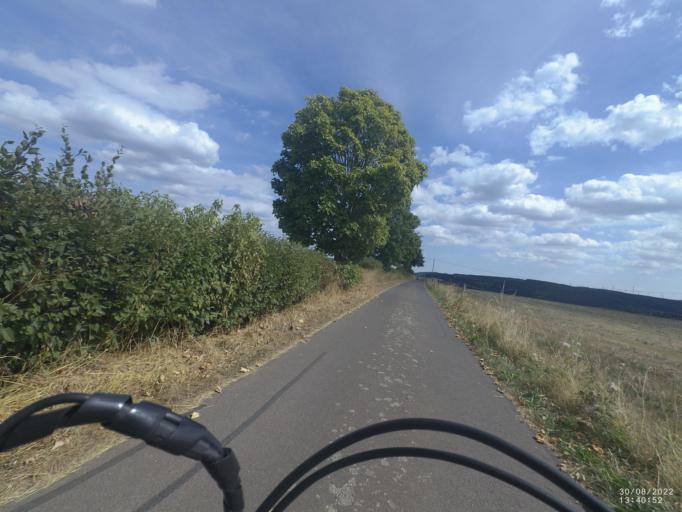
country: DE
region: Rheinland-Pfalz
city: Scheid
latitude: 50.3569
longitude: 6.4193
